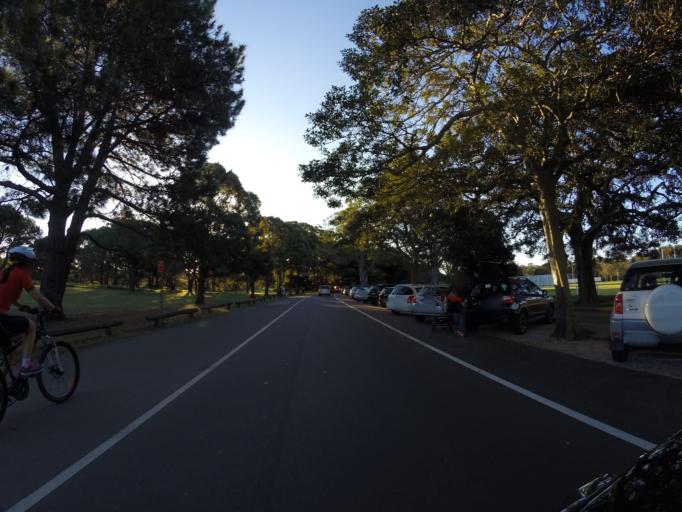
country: AU
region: New South Wales
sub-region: Woollahra
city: Woollahra
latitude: -33.9013
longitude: 151.2284
